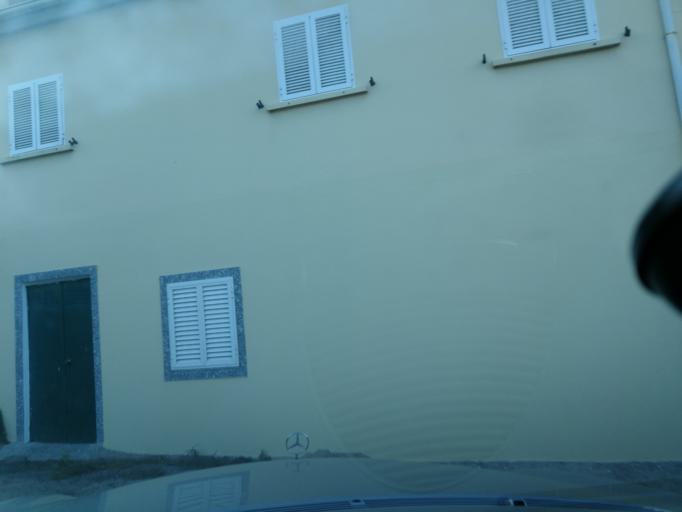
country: PT
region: Braga
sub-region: Braga
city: Braga
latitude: 41.5294
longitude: -8.4292
